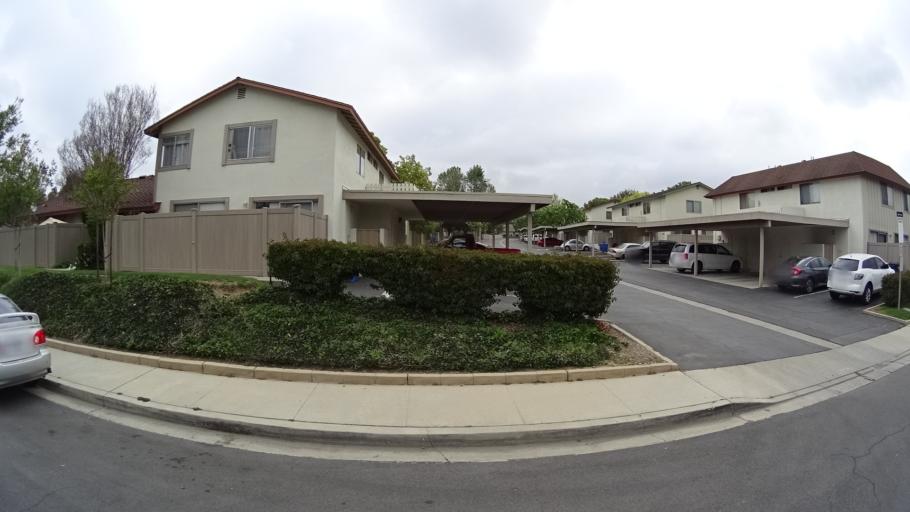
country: US
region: California
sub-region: Ventura County
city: Thousand Oaks
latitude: 34.2083
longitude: -118.8476
